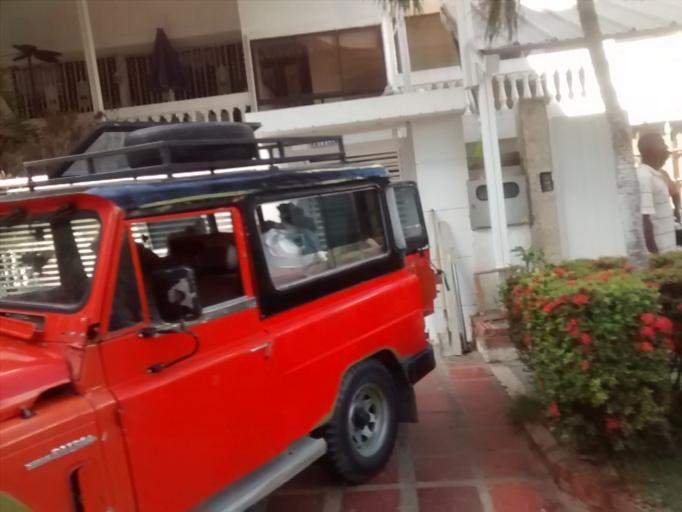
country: CO
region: Bolivar
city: Cartagena
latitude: 10.3951
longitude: -75.5525
